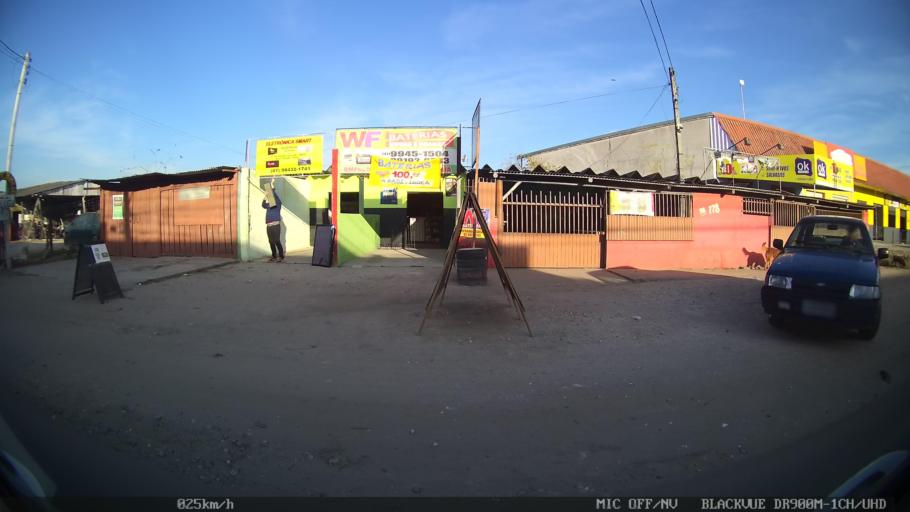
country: BR
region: Parana
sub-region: Pinhais
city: Pinhais
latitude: -25.4548
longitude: -49.1527
